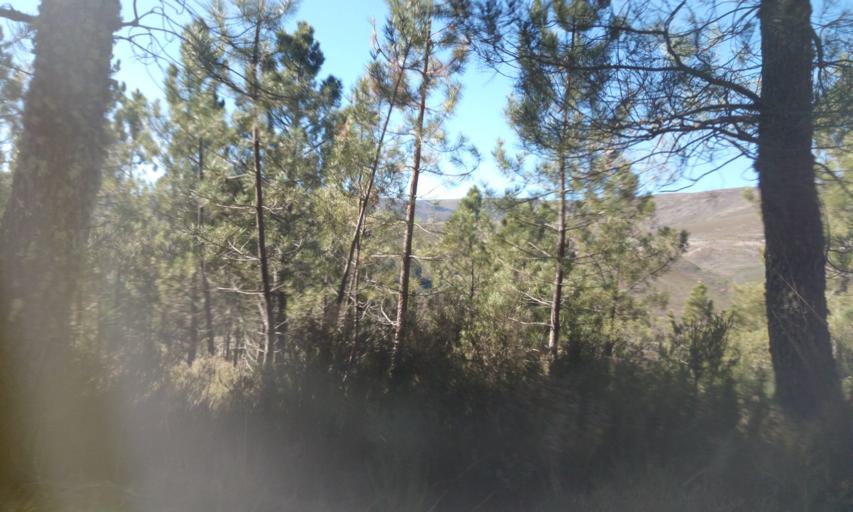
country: PT
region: Guarda
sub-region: Manteigas
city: Manteigas
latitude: 40.4466
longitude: -7.5081
